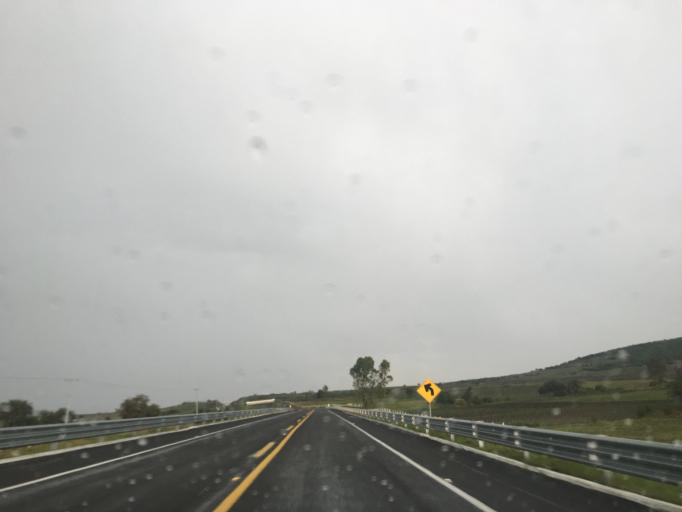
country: MX
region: Michoacan
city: Alvaro Obregon
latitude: 19.8113
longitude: -101.0154
